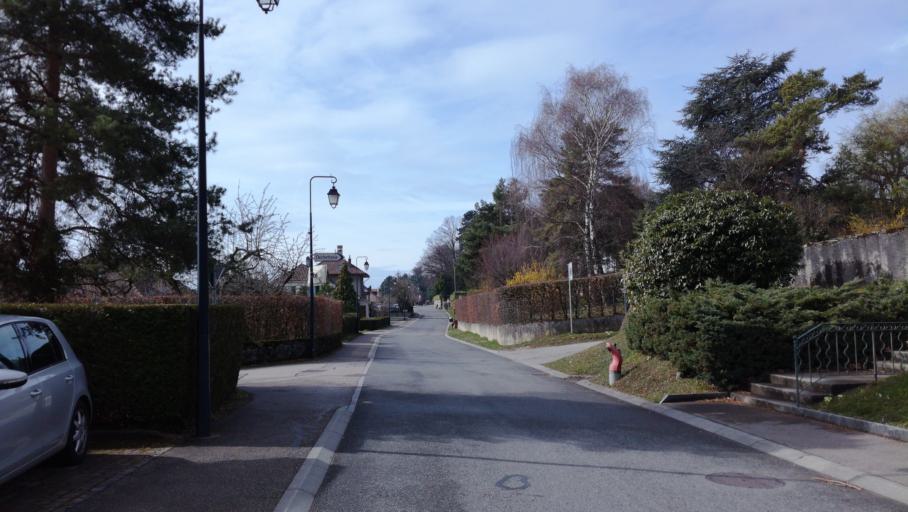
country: CH
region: Vaud
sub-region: Nyon District
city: Rolle
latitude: 46.4377
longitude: 6.3040
